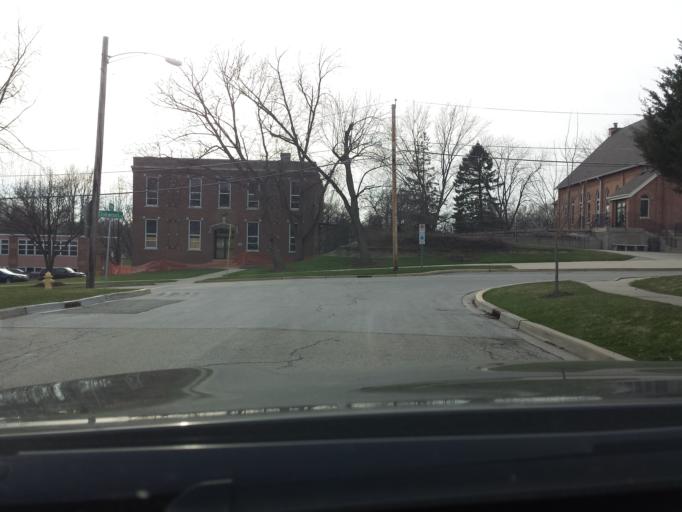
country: US
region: Illinois
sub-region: DuPage County
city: West Chicago
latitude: 41.8868
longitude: -88.1990
